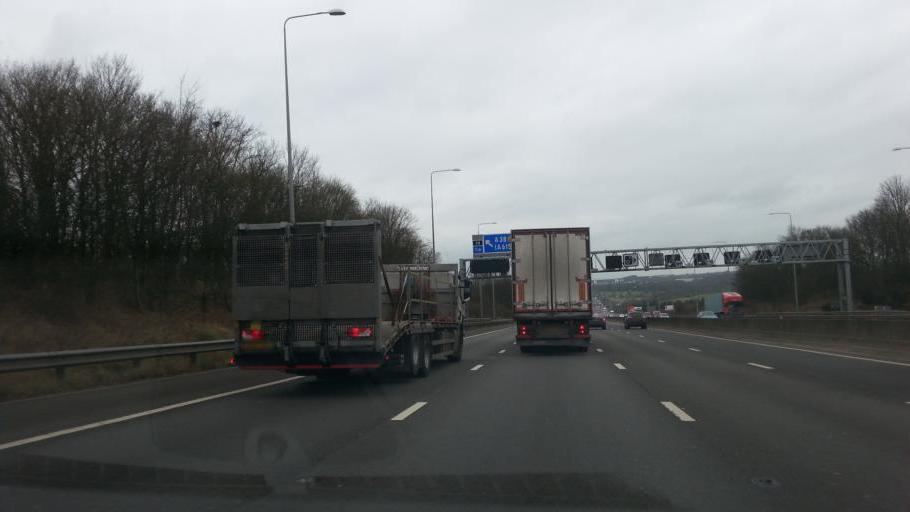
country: GB
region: England
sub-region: Derbyshire
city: Pinxton
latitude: 53.0828
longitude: -1.2979
